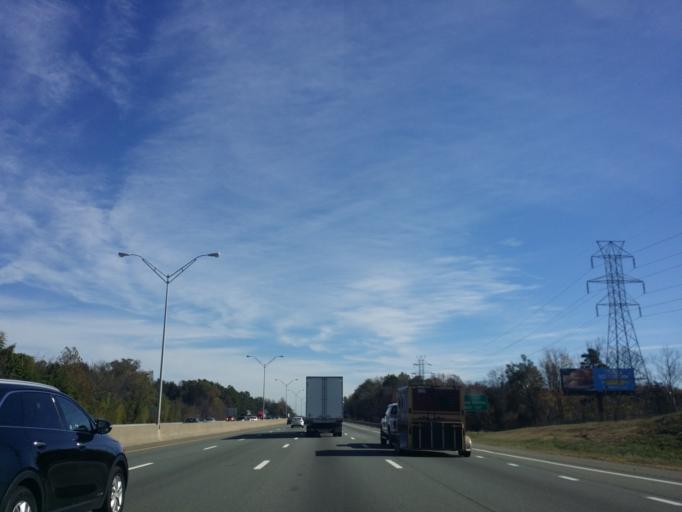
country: US
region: North Carolina
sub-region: Alamance County
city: Burlington
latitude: 36.0645
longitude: -79.4620
